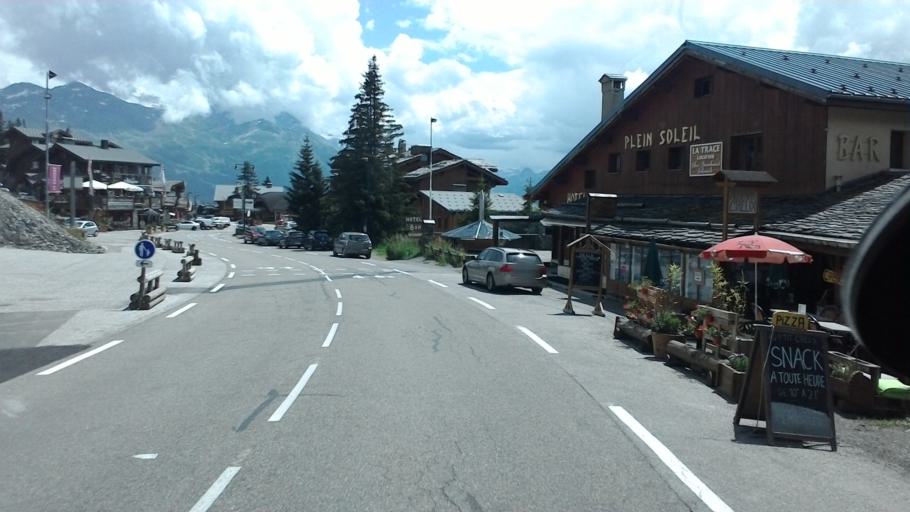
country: FR
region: Rhone-Alpes
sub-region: Departement de la Savoie
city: Seez
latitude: 45.6280
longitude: 6.8485
